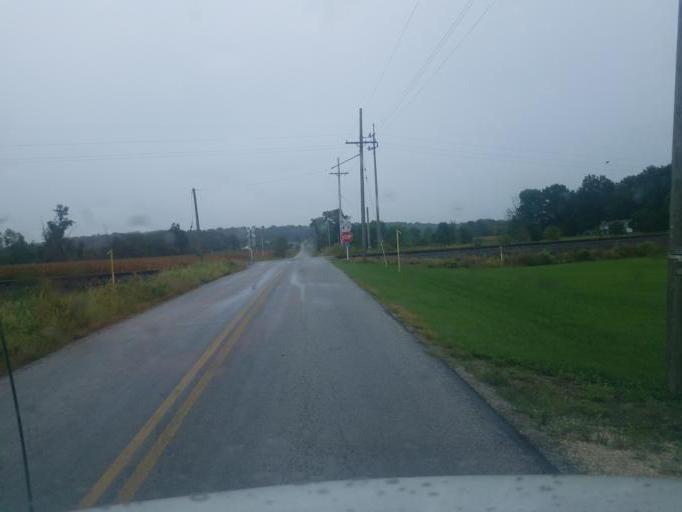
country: US
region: Ohio
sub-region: Medina County
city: Seville
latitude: 40.9824
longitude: -81.8538
